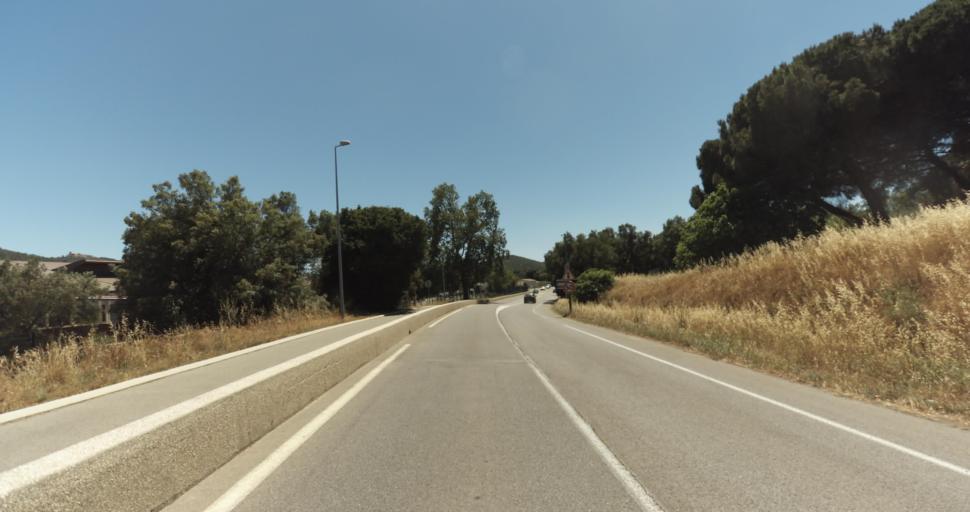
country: FR
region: Provence-Alpes-Cote d'Azur
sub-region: Departement du Var
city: Gassin
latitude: 43.2477
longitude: 6.5723
